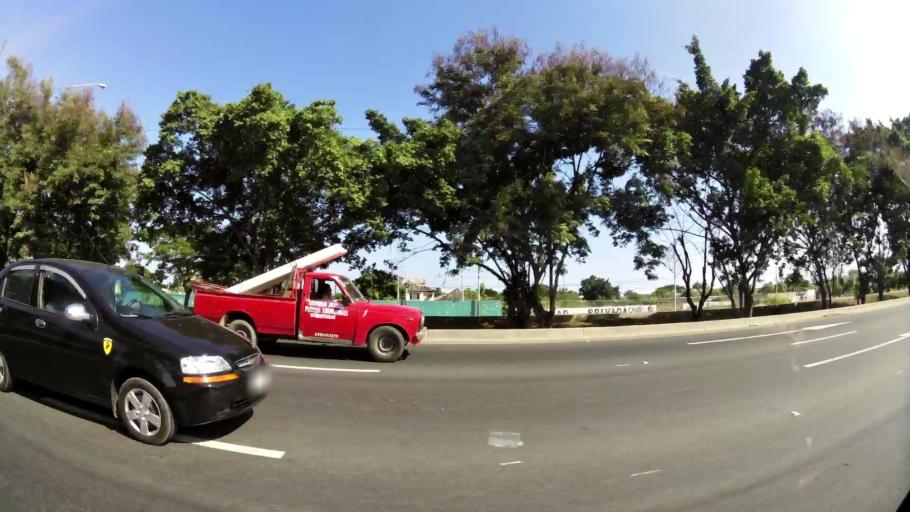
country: EC
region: Guayas
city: Santa Lucia
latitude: -2.1850
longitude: -79.9723
